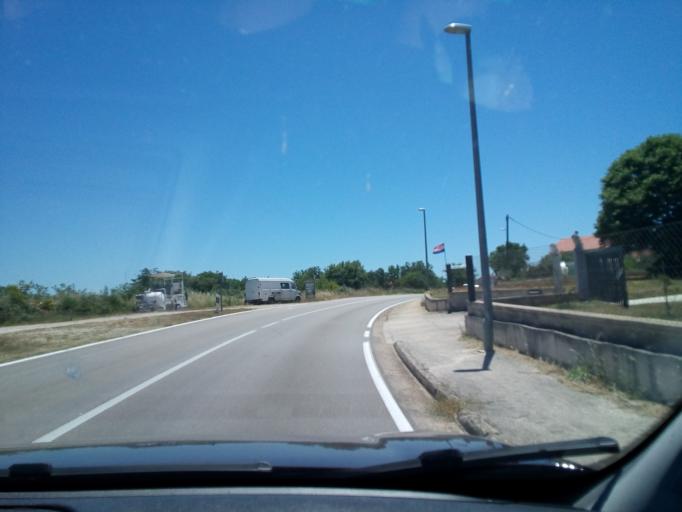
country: HR
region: Zadarska
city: Zadar
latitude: 44.1754
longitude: 15.2891
